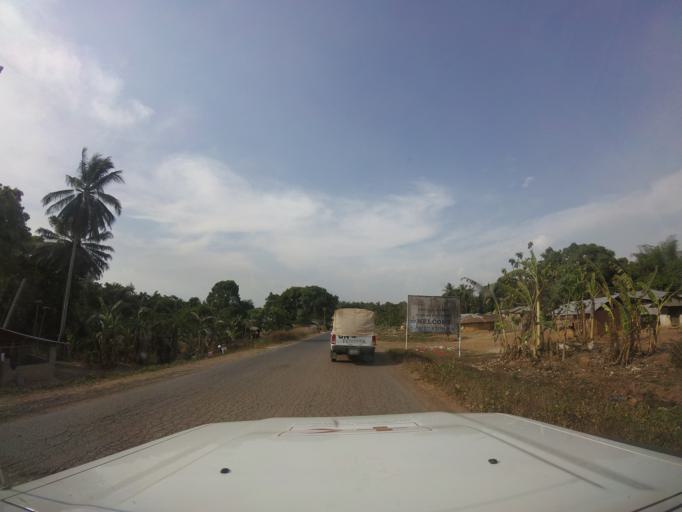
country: LR
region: Bomi
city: Tubmanburg
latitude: 6.7841
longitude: -10.8455
